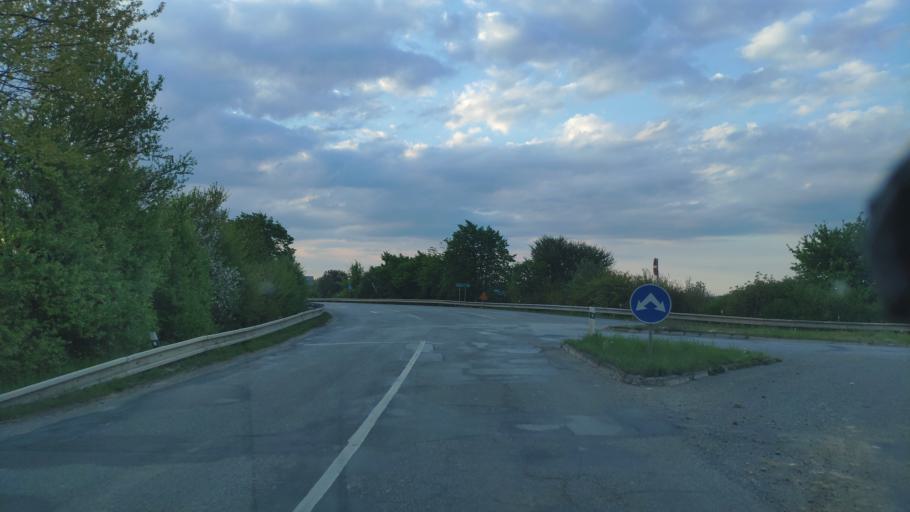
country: SK
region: Presovsky
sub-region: Okres Presov
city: Presov
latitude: 48.9508
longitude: 21.2589
